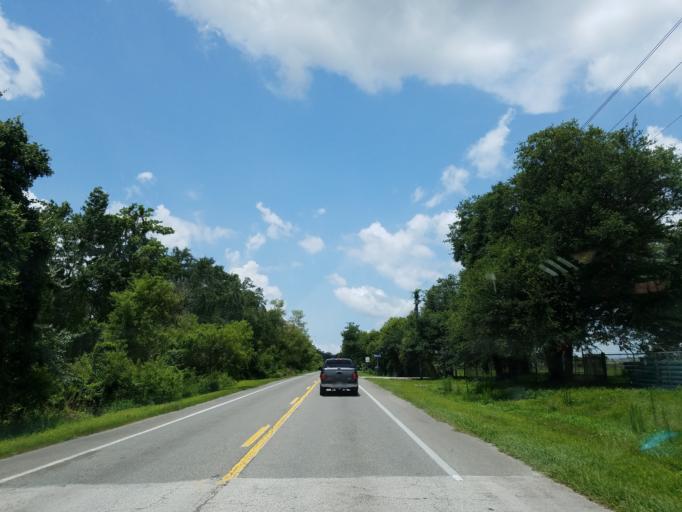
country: US
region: Florida
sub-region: Hillsborough County
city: Fish Hawk
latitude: 27.8506
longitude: -82.1199
